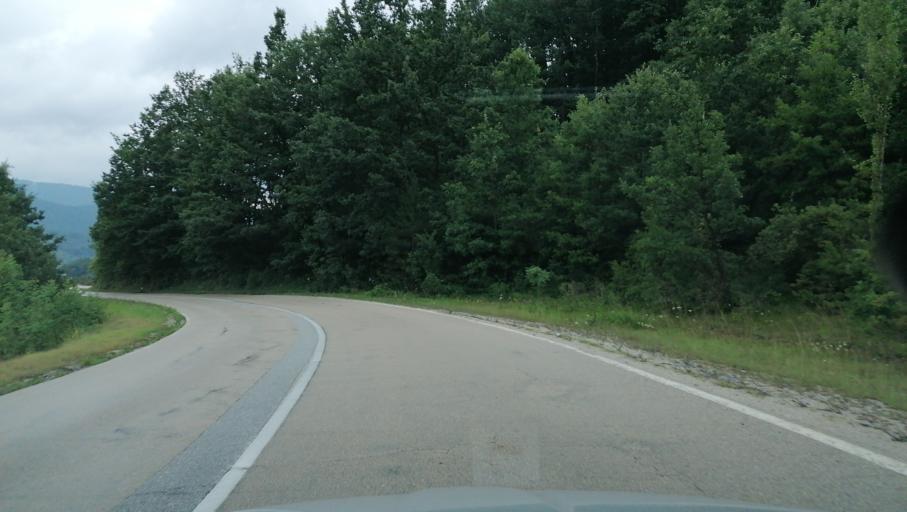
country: RS
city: Durici
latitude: 43.8039
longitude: 19.5110
